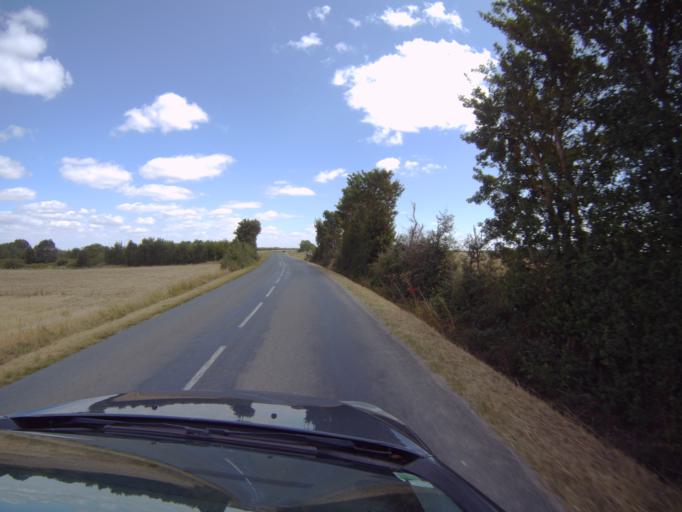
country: FR
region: Poitou-Charentes
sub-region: Departement de la Charente-Maritime
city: Saint-Jean-de-Liversay
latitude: 46.2616
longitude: -0.8674
